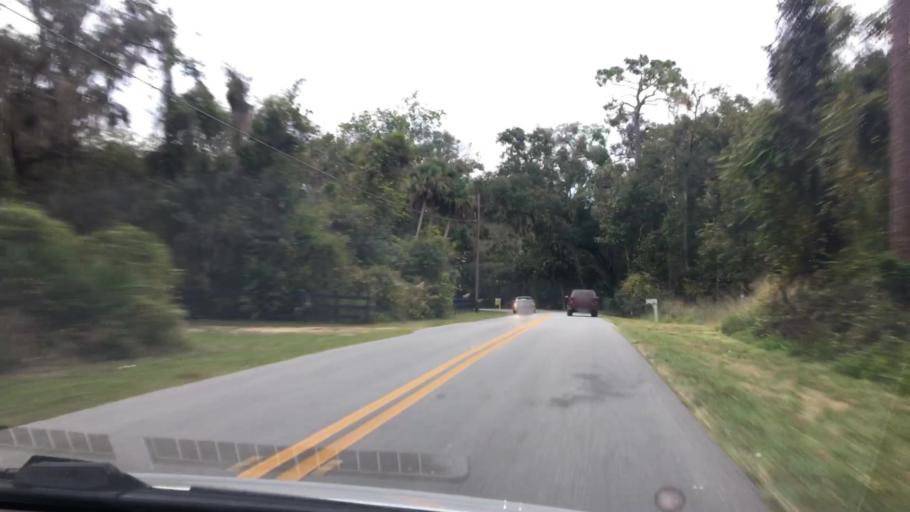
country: US
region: Florida
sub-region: Seminole County
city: Midway
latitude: 28.8557
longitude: -81.2099
